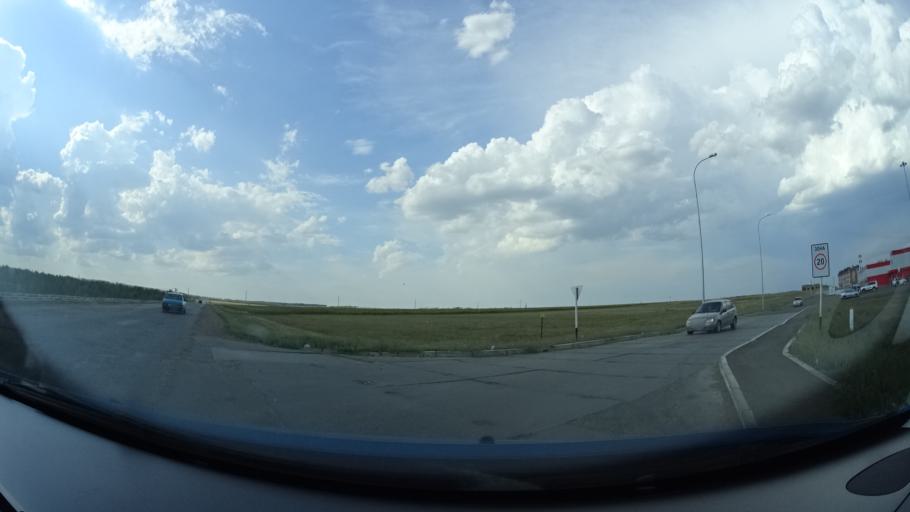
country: RU
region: Bashkortostan
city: Meleuz
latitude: 52.9653
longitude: 55.9080
